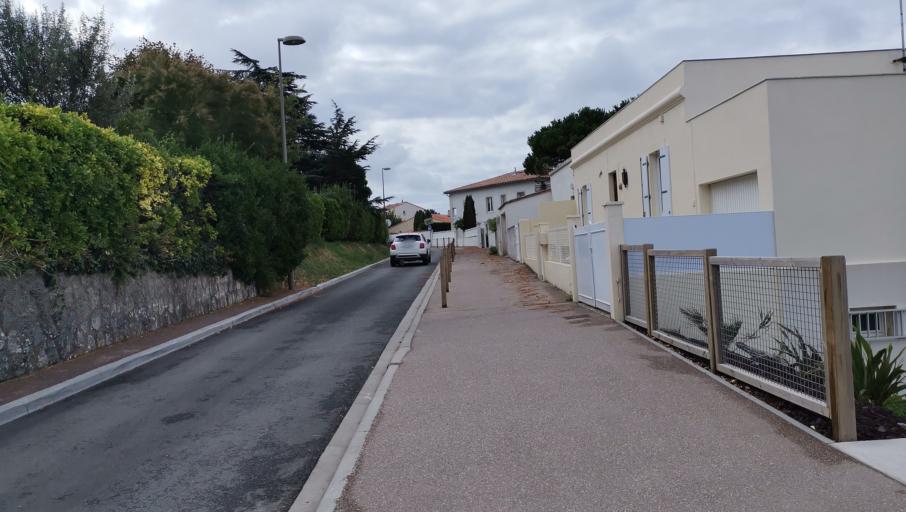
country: FR
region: Poitou-Charentes
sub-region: Departement de la Charente-Maritime
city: Meschers-sur-Gironde
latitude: 45.5585
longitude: -0.9627
